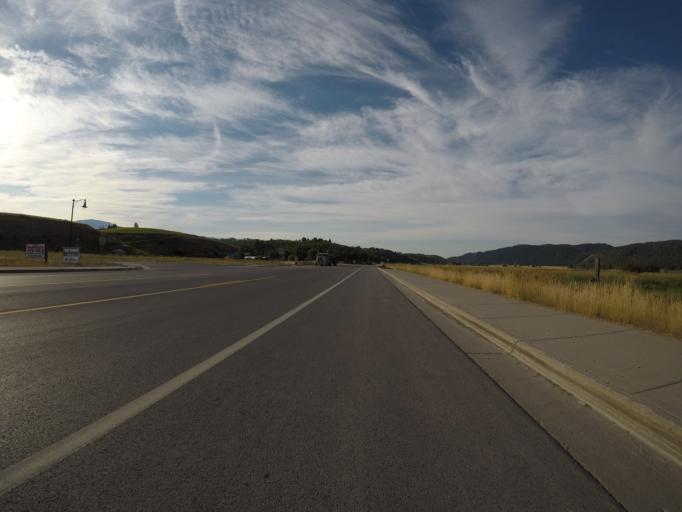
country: US
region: Wyoming
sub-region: Lincoln County
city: Afton
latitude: 42.9134
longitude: -111.0002
